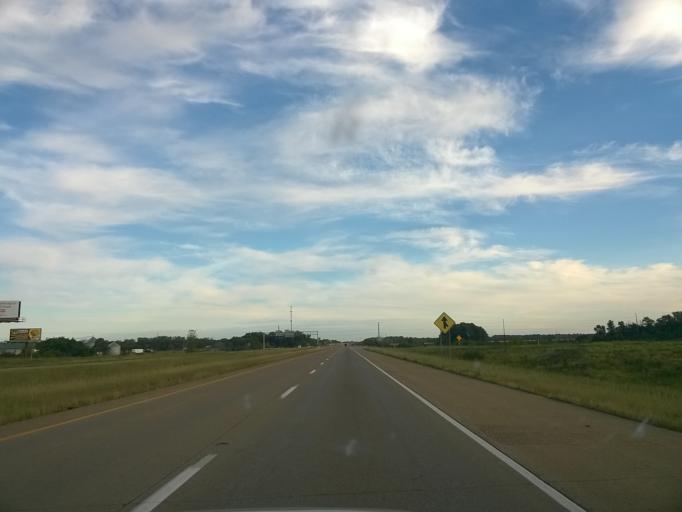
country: US
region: Indiana
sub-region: Vanderburgh County
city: Melody Hill
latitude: 38.0164
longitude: -87.4697
